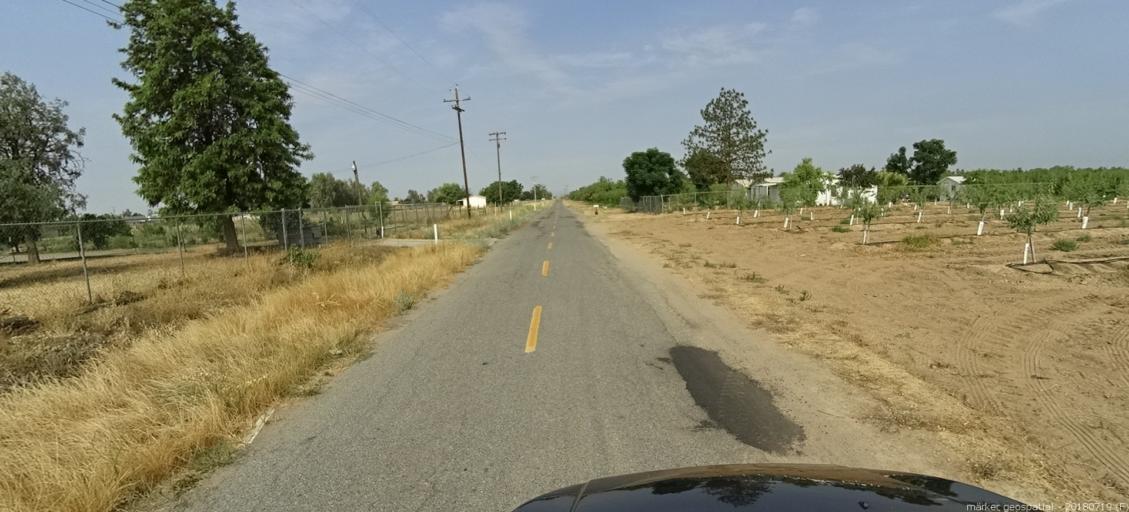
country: US
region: California
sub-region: Madera County
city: Fairmead
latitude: 37.0910
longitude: -120.1879
